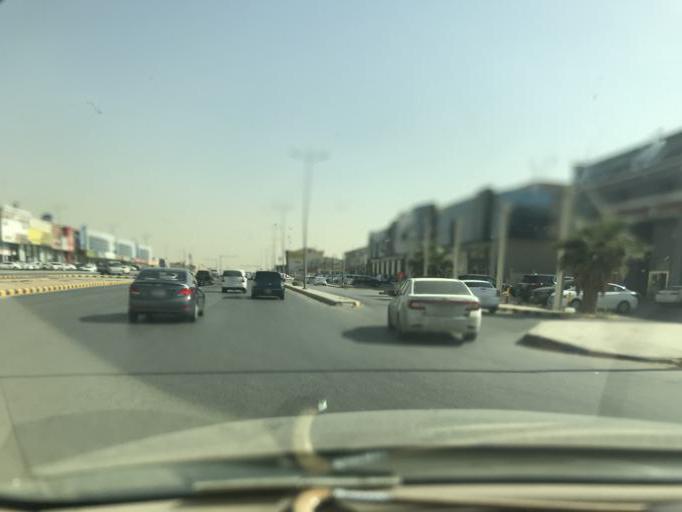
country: SA
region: Ar Riyad
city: Riyadh
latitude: 24.8035
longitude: 46.7385
